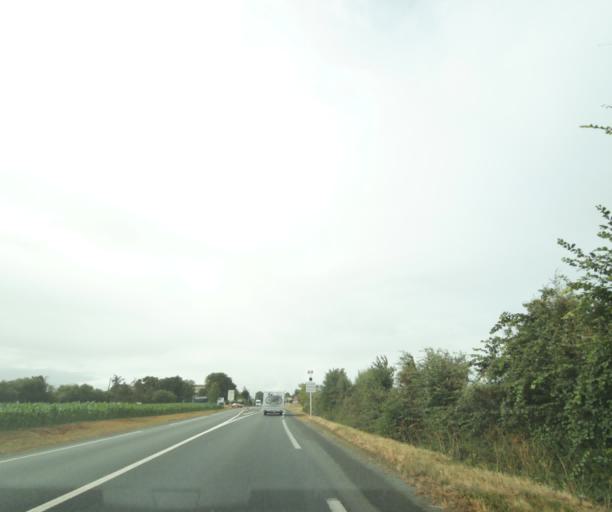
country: FR
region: Pays de la Loire
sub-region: Departement de la Vendee
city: Sainte-Gemme-la-Plaine
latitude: 46.4528
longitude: -1.1044
